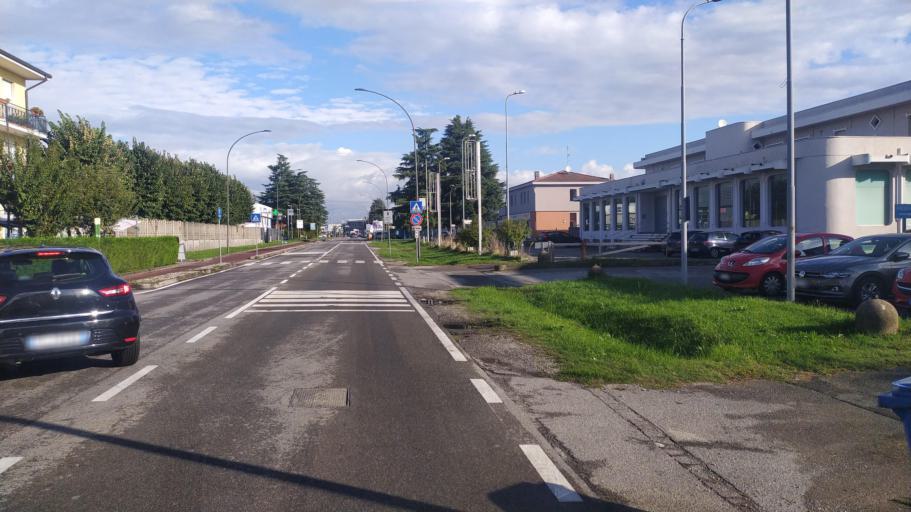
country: IT
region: Lombardy
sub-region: Citta metropolitana di Milano
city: Cernusco sul Naviglio
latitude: 45.5336
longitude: 9.3373
